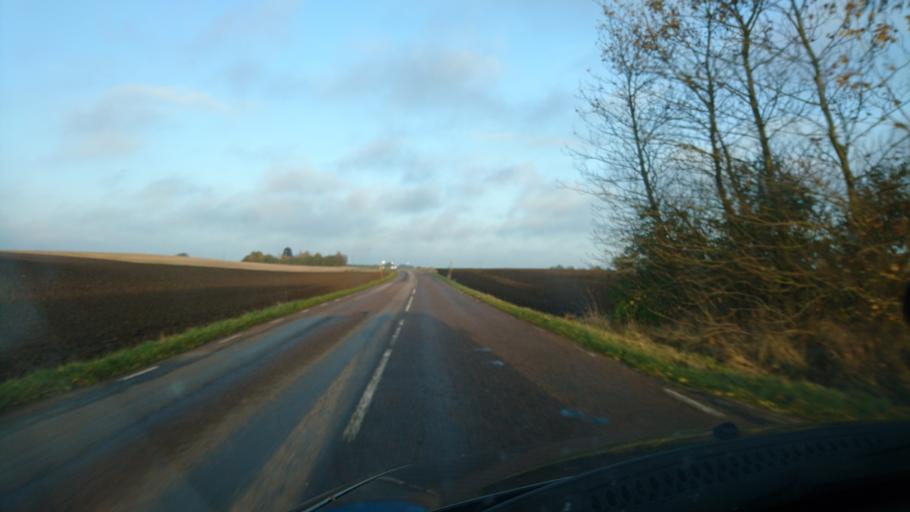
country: SE
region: Skane
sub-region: Ystads Kommun
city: Kopingebro
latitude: 55.4479
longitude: 14.1406
